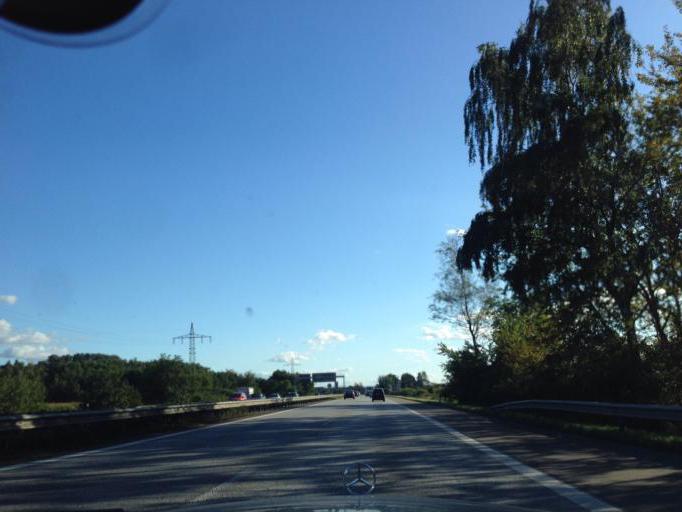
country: DE
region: Schleswig-Holstein
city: Padenstedt
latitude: 54.0678
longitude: 9.9224
